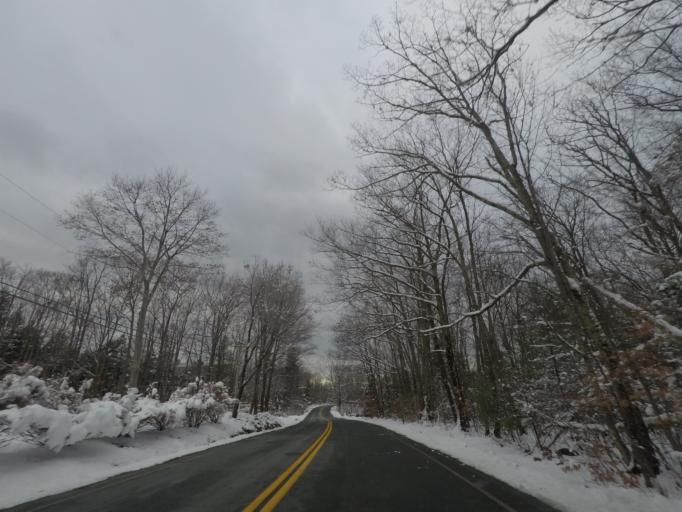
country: US
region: New York
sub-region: Rensselaer County
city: Averill Park
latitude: 42.6688
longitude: -73.5235
